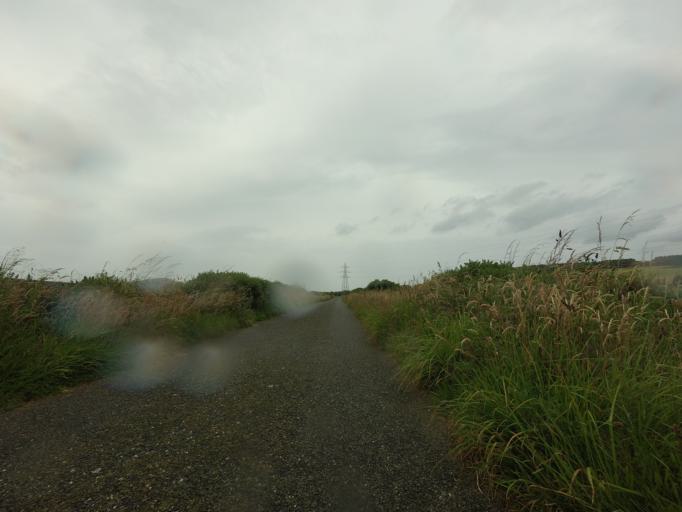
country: GB
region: Scotland
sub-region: Moray
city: Cullen
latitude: 57.6738
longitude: -2.7880
